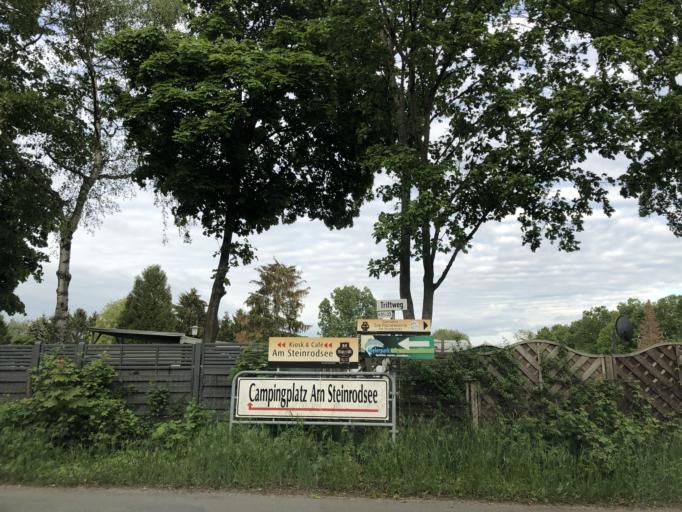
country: DE
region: Hesse
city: Weiterstadt
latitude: 49.9429
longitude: 8.6034
